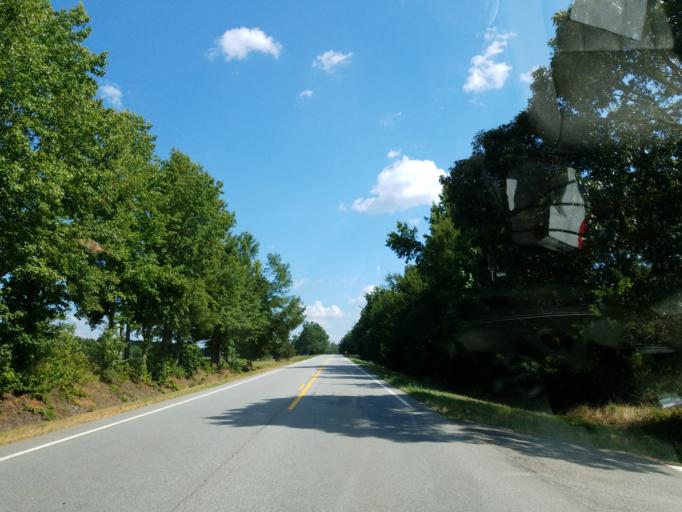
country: US
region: Georgia
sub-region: Lamar County
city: Barnesville
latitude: 32.9624
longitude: -84.1109
